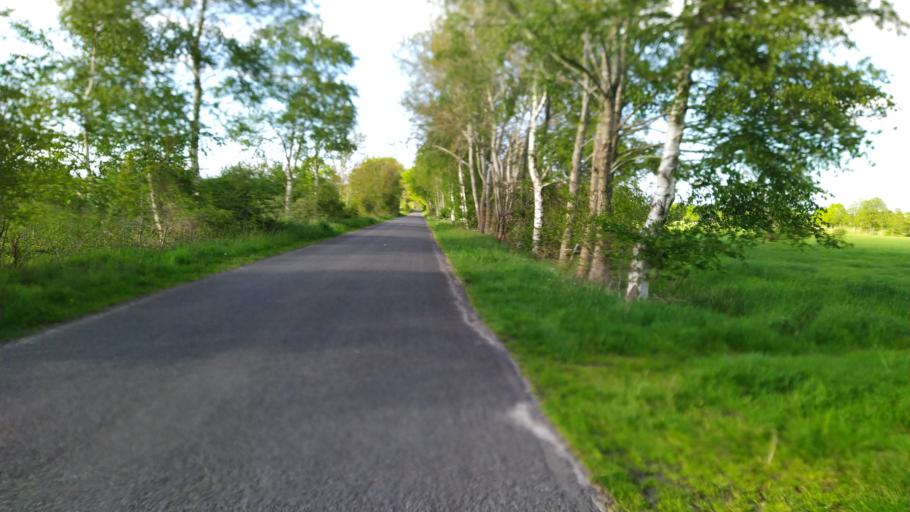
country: DE
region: Lower Saxony
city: Farven
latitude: 53.4224
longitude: 9.3368
